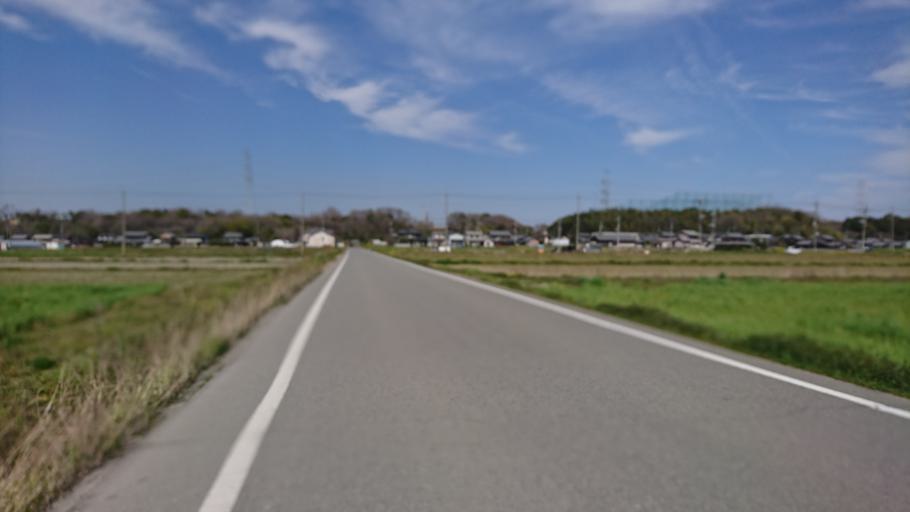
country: JP
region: Hyogo
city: Miki
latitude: 34.7729
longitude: 134.9361
